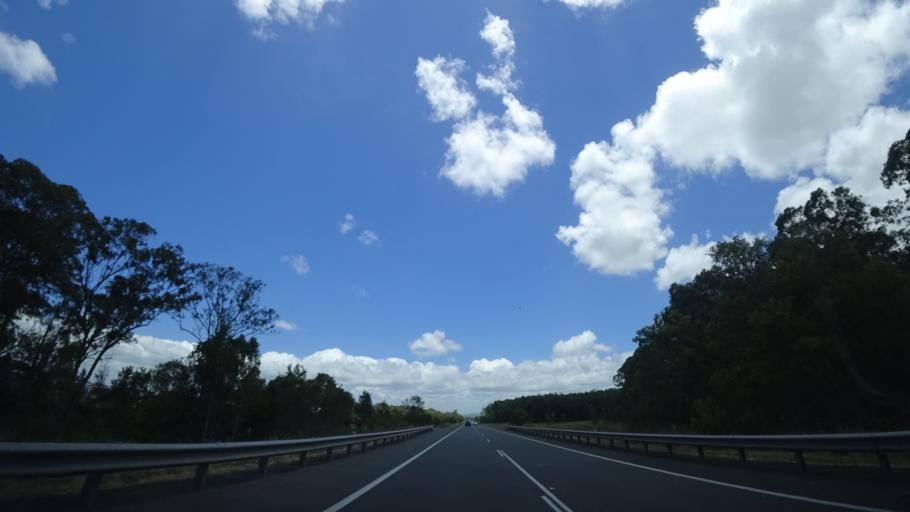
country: AU
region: Queensland
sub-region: Sunshine Coast
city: Little Mountain
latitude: -26.7656
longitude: 153.1003
